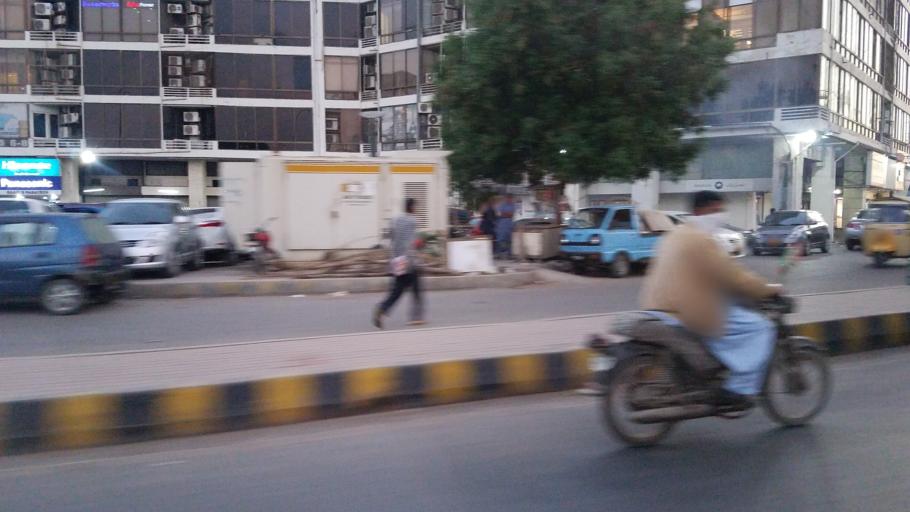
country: PK
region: Sindh
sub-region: Karachi District
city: Karachi
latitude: 24.8275
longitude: 67.0342
